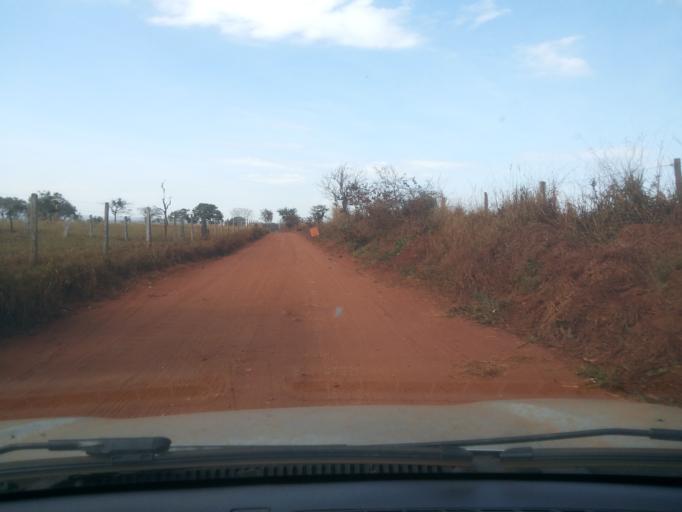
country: BR
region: Minas Gerais
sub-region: Ituiutaba
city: Ituiutaba
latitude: -19.0220
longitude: -49.3952
